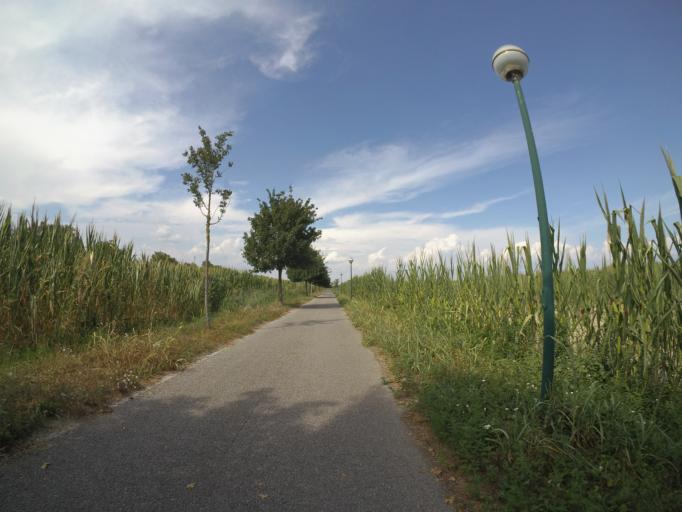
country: IT
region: Veneto
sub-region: Provincia di Venezia
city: Bibione
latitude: 45.6685
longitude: 13.0703
